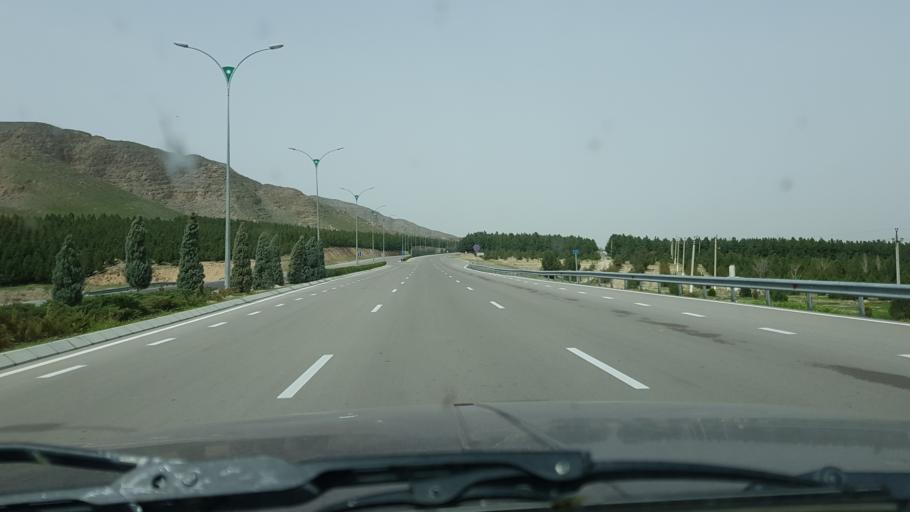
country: TM
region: Ahal
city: Abadan
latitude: 37.9378
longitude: 58.2065
